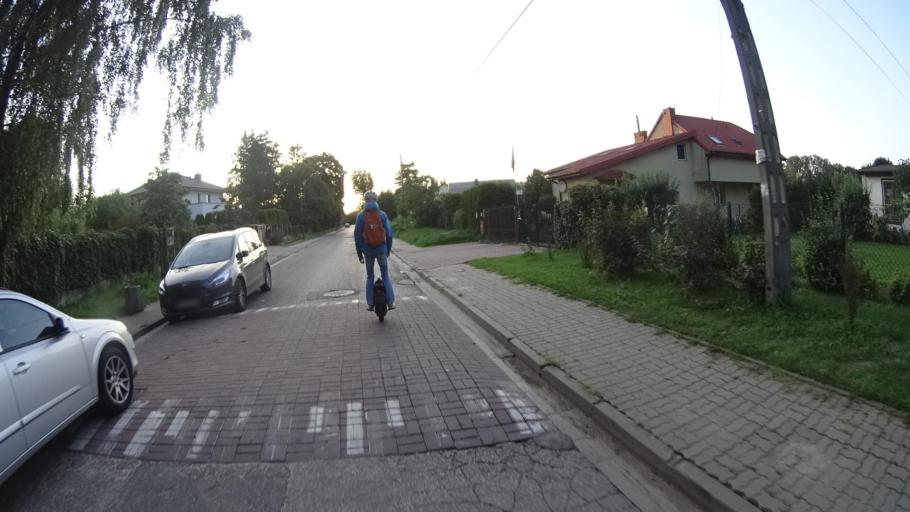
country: PL
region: Masovian Voivodeship
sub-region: Warszawa
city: Bielany
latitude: 52.3060
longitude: 20.9387
